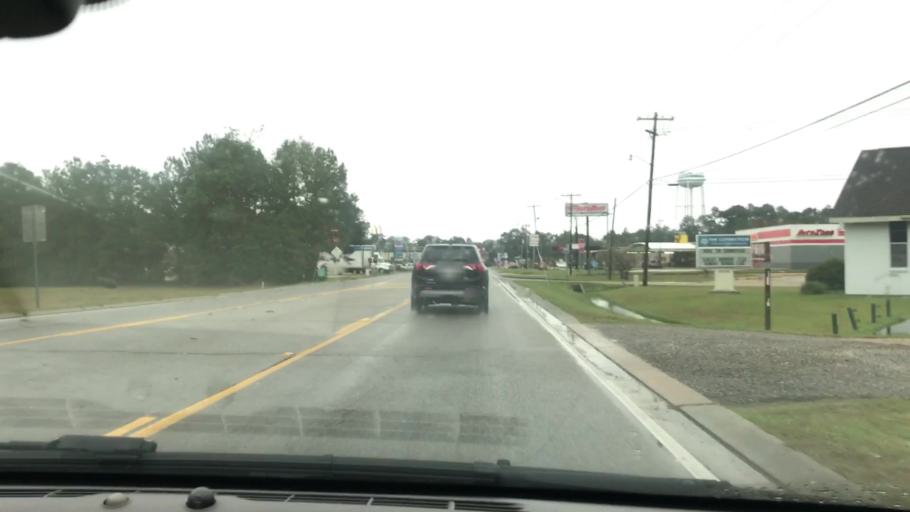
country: US
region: Louisiana
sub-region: Saint Tammany Parish
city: Pearl River
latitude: 30.3618
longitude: -89.7529
